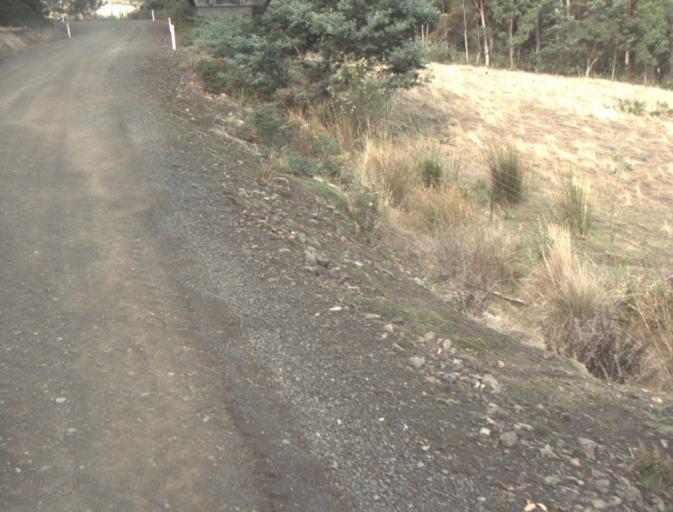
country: AU
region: Tasmania
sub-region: Launceston
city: Mayfield
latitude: -41.2162
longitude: 147.1707
